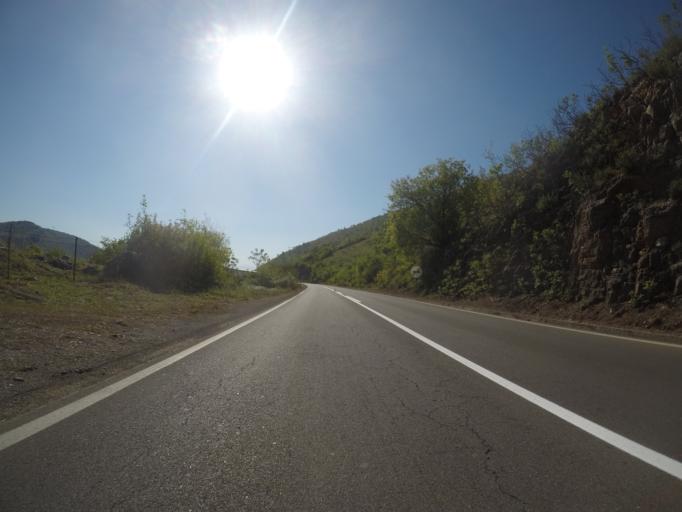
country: ME
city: Spuz
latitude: 42.4581
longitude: 19.1801
